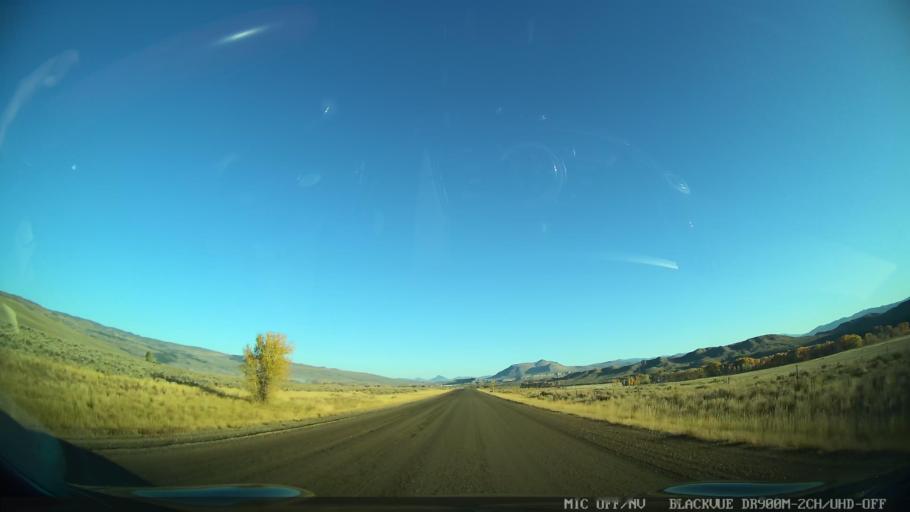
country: US
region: Colorado
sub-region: Grand County
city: Kremmling
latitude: 40.0223
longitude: -106.3891
